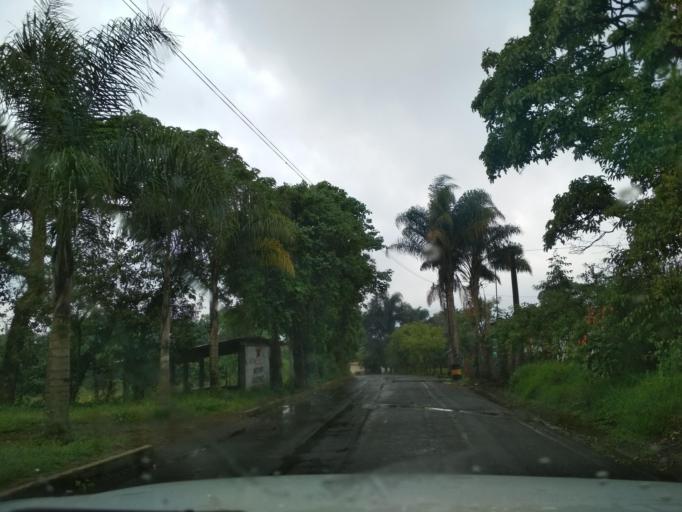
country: MX
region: Veracruz
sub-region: Ixhuatlancillo
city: San Isidro
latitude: 18.9009
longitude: -97.1208
